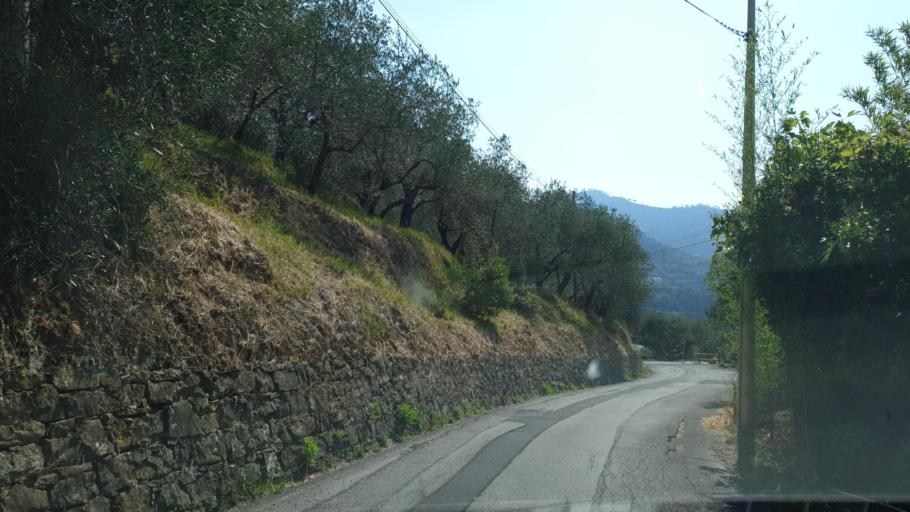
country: IT
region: Liguria
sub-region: Provincia di La Spezia
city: Levanto
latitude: 44.1806
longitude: 9.6184
